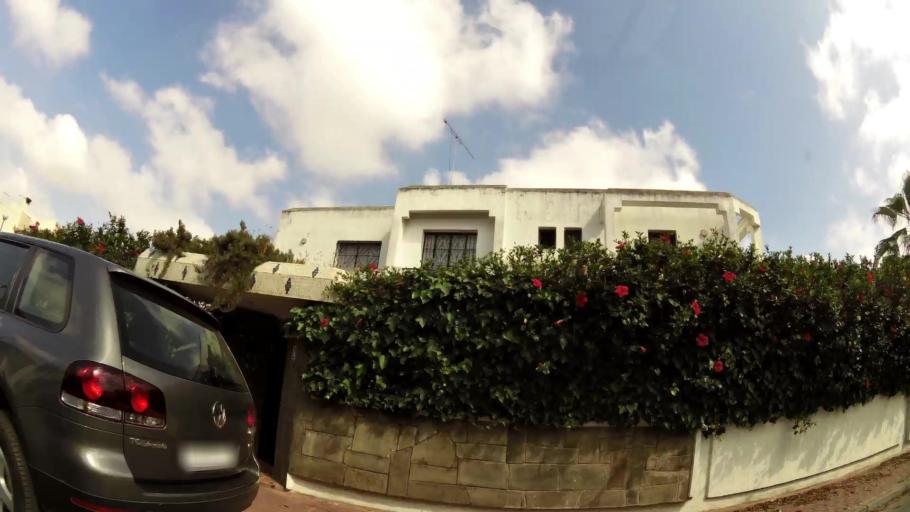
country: MA
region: Rabat-Sale-Zemmour-Zaer
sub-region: Skhirate-Temara
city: Temara
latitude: 33.9633
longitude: -6.8635
